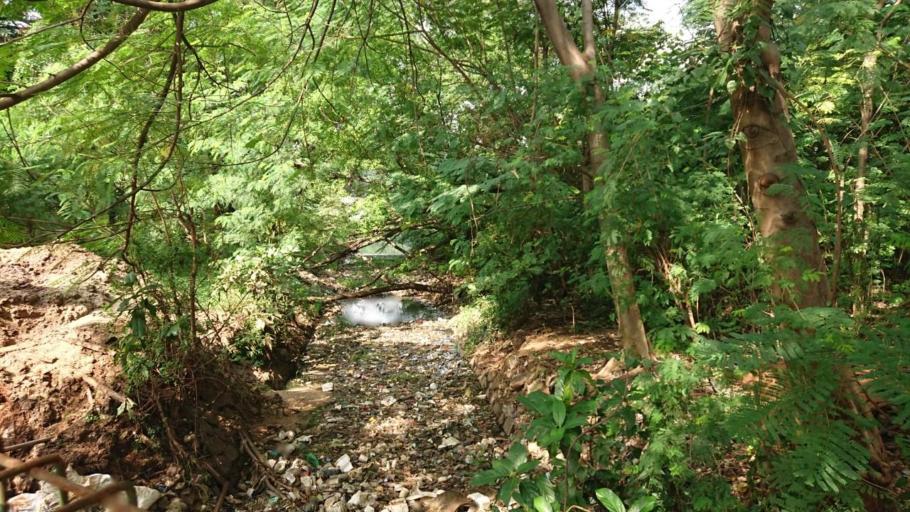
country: ID
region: Jakarta Raya
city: Jakarta
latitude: -6.2020
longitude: 106.9128
